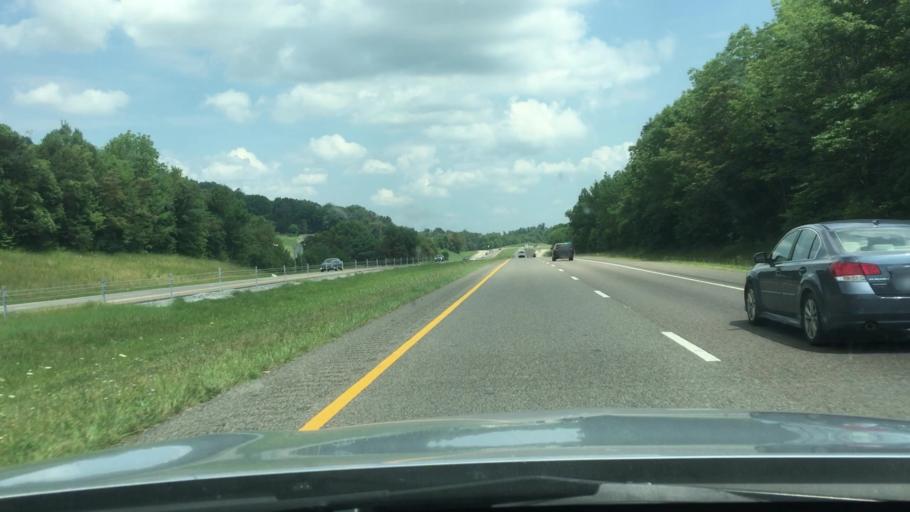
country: US
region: Tennessee
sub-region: Carter County
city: Pine Crest
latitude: 36.2609
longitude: -82.3223
